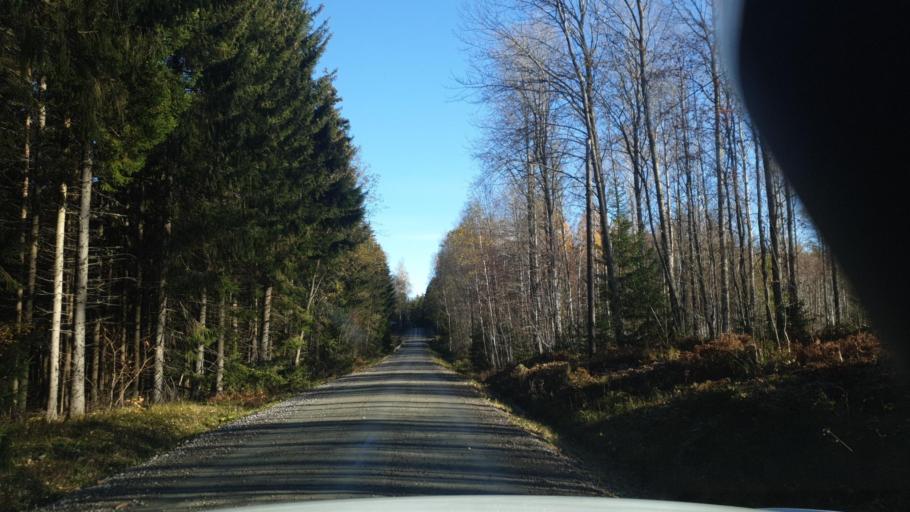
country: SE
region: Vaermland
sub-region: Karlstads Kommun
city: Edsvalla
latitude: 59.5041
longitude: 13.1984
